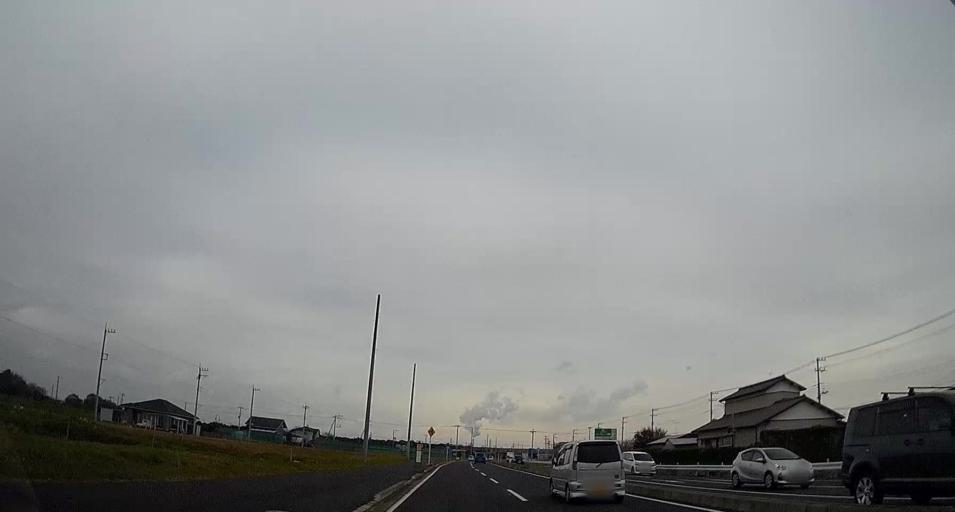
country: JP
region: Chiba
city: Kisarazu
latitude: 35.4261
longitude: 139.9227
